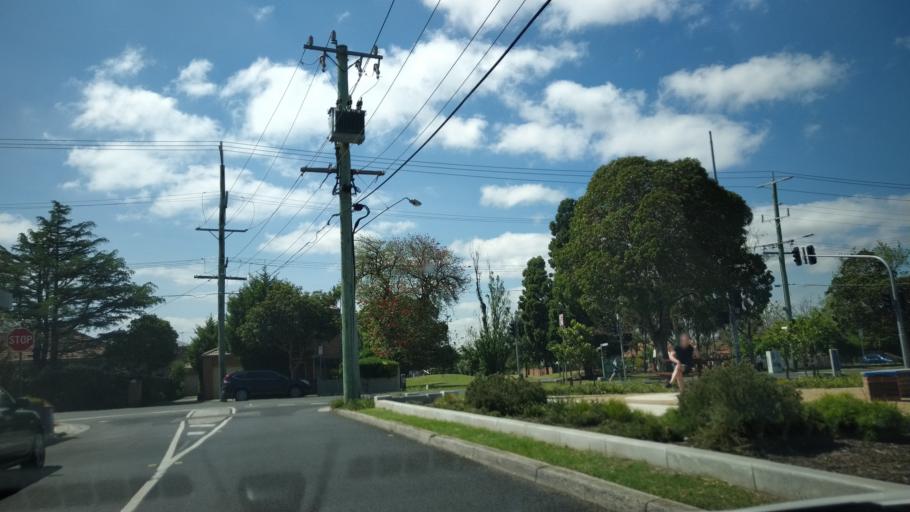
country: AU
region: Victoria
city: Ormond
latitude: -37.8967
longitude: 145.0358
